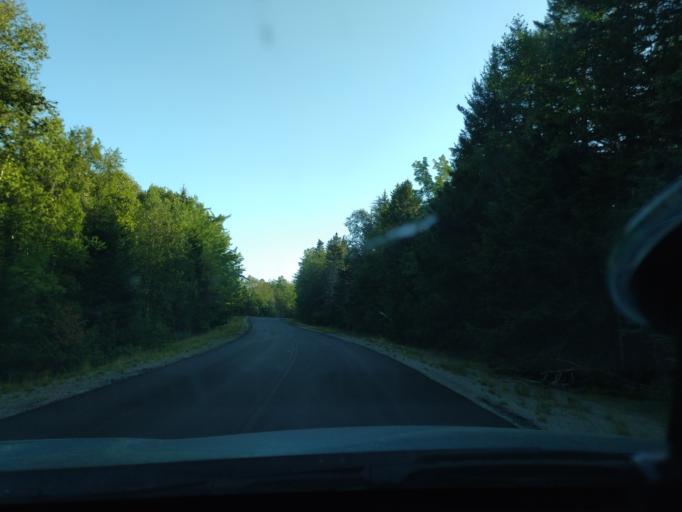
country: US
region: Maine
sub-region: Washington County
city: East Machias
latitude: 44.7100
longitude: -67.1441
